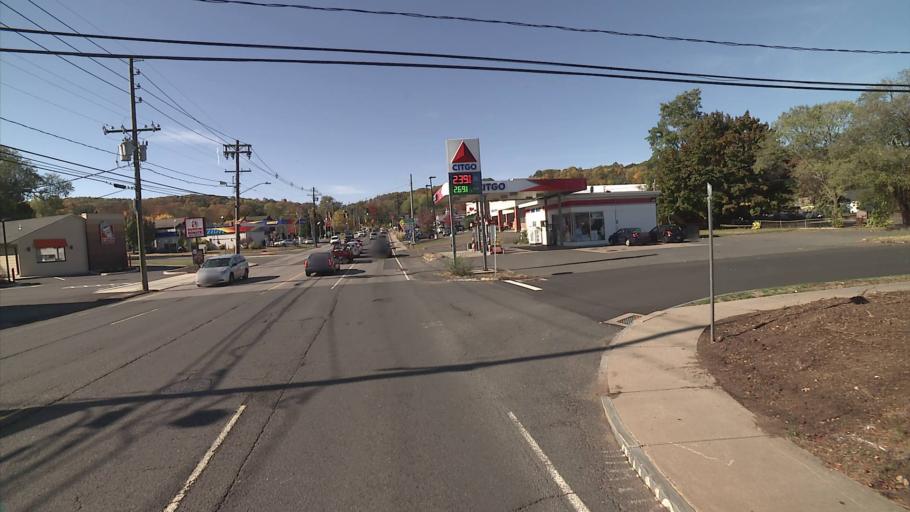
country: US
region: Connecticut
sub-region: Hartford County
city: Bristol
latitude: 41.6903
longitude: -72.9248
